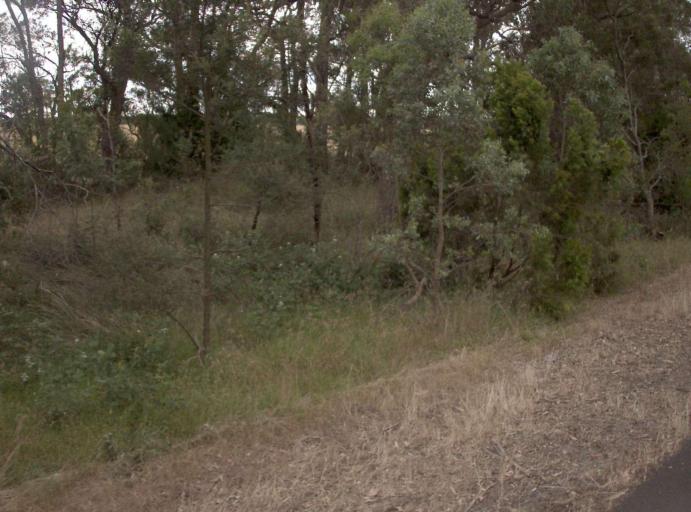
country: AU
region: Victoria
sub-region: Wellington
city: Sale
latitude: -38.3618
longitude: 146.9918
